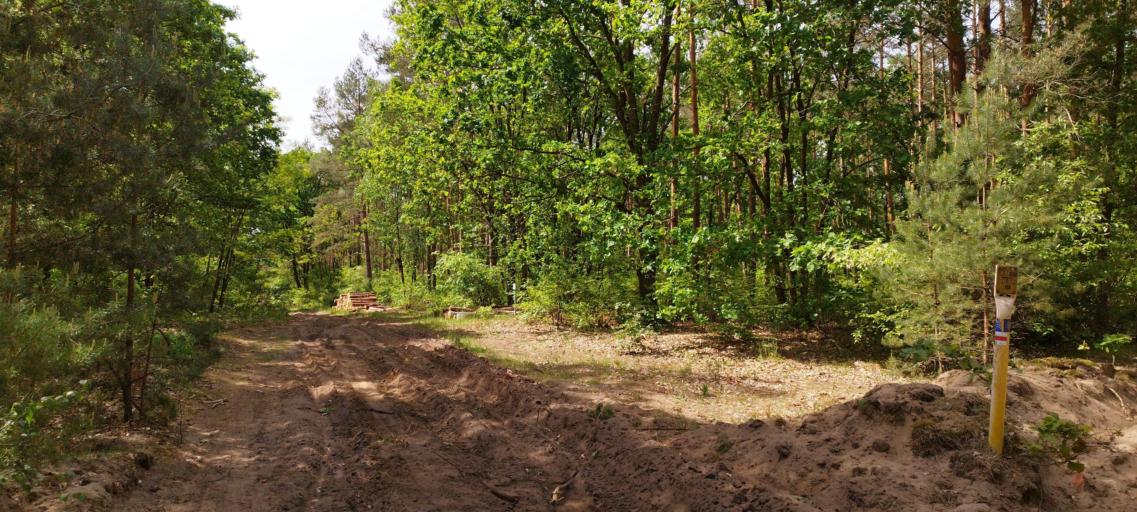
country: DE
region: Brandenburg
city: Furstenwalde
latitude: 52.3621
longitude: 14.0308
